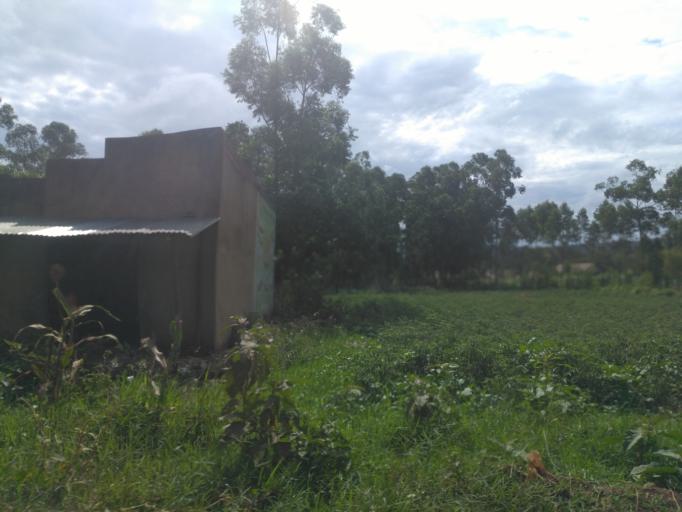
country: UG
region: Central Region
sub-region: Buikwe District
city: Njeru
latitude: 0.3977
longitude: 33.1747
